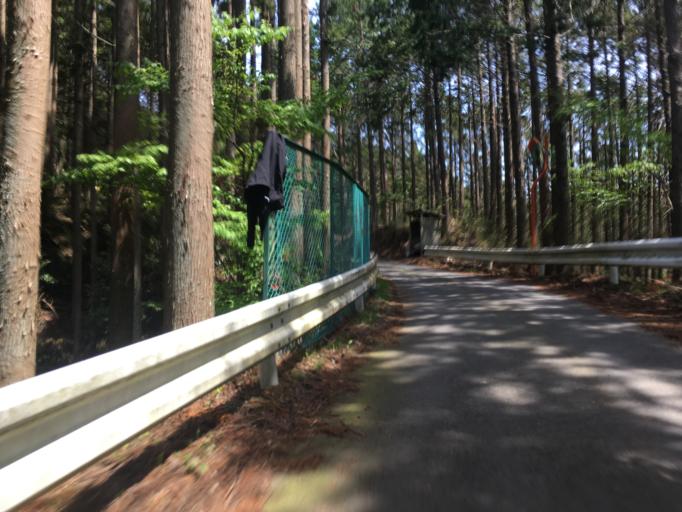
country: JP
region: Kyoto
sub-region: Kyoto-shi
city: Kamigyo-ku
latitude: 35.0753
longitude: 135.7183
